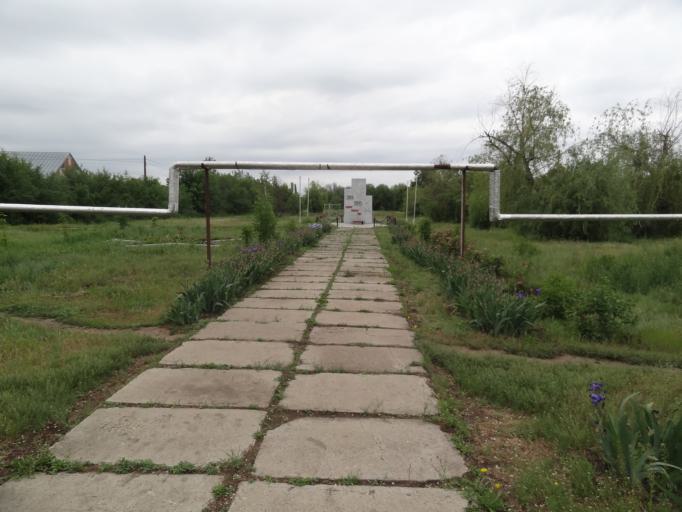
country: RU
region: Saratov
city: Shumeyka
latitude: 51.3608
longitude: 46.2819
